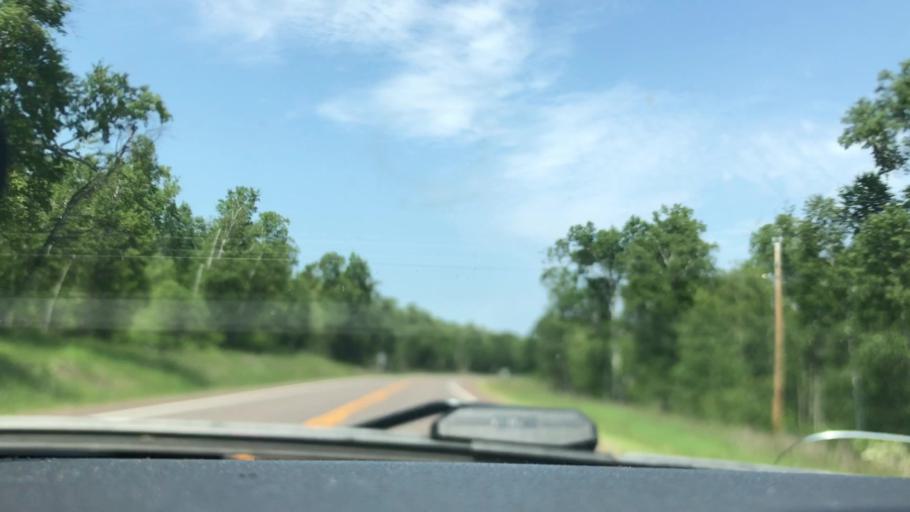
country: US
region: Minnesota
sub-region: Lake County
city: Silver Bay
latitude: 47.4968
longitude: -90.9711
